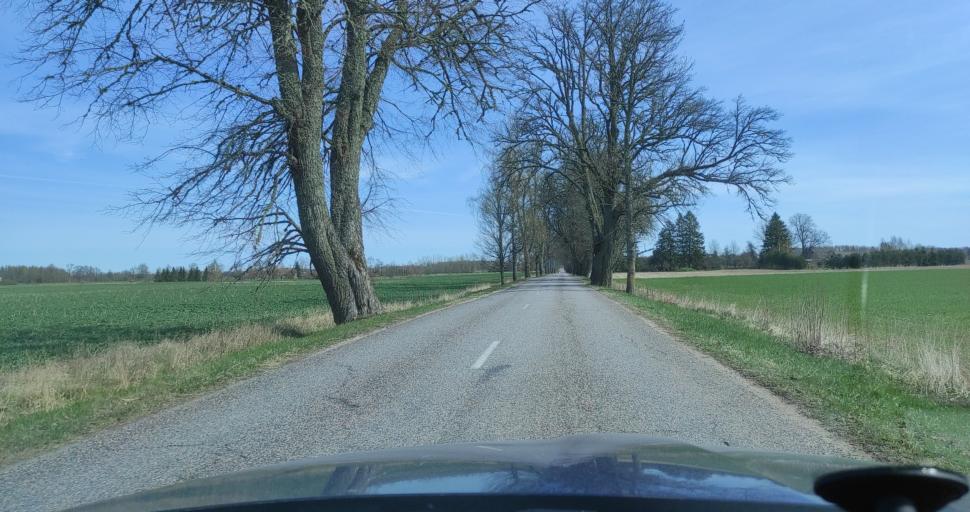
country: LV
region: Talsu Rajons
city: Stende
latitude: 57.2158
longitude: 22.5003
